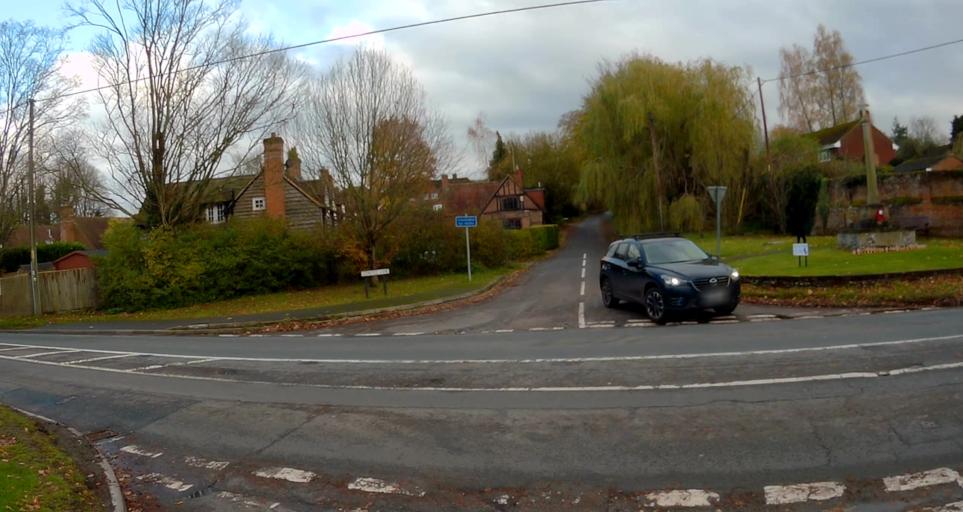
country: GB
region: England
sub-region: Hampshire
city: Long Sutton
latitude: 51.2209
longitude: -0.9676
